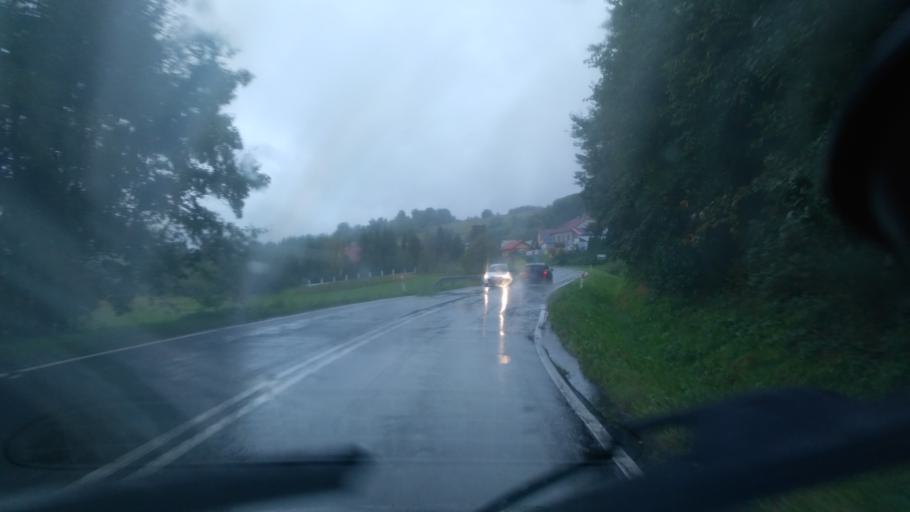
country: PL
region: Subcarpathian Voivodeship
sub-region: Powiat ropczycko-sedziszowski
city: Niedzwiada
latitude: 49.9897
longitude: 21.5624
